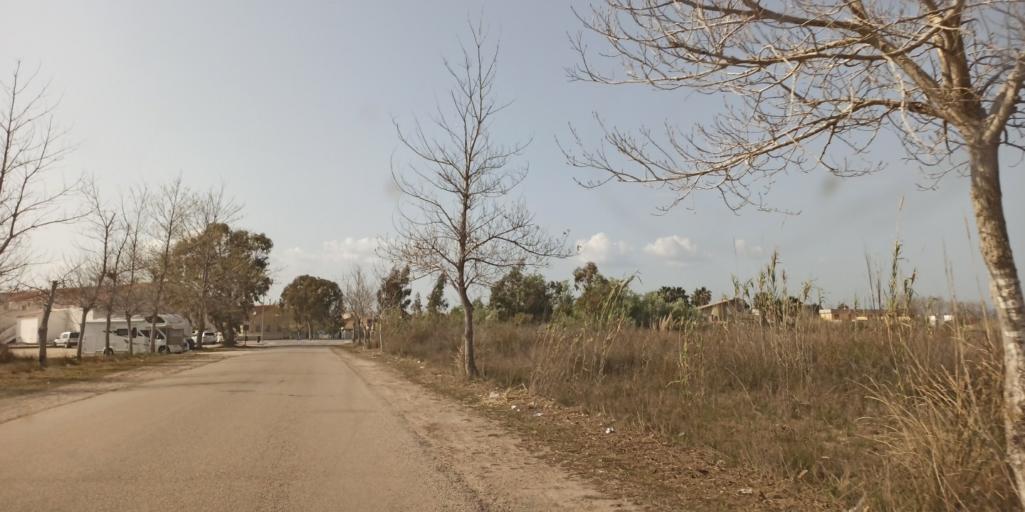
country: ES
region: Catalonia
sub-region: Provincia de Tarragona
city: Deltebre
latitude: 40.7228
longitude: 0.8439
